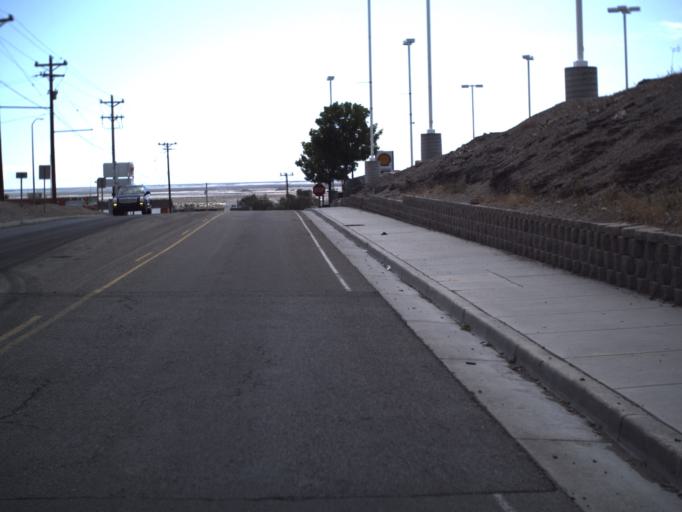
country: US
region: Utah
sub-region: Tooele County
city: Wendover
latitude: 40.7374
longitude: -114.0427
